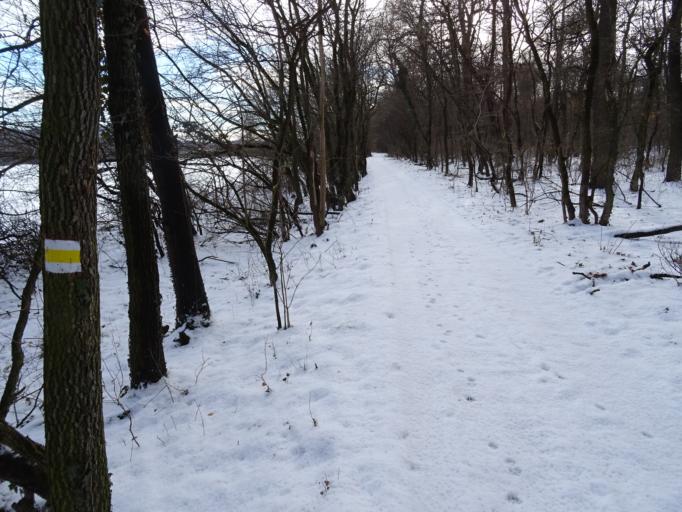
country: HU
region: Komarom-Esztergom
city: Oroszlany
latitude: 47.4949
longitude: 18.3380
